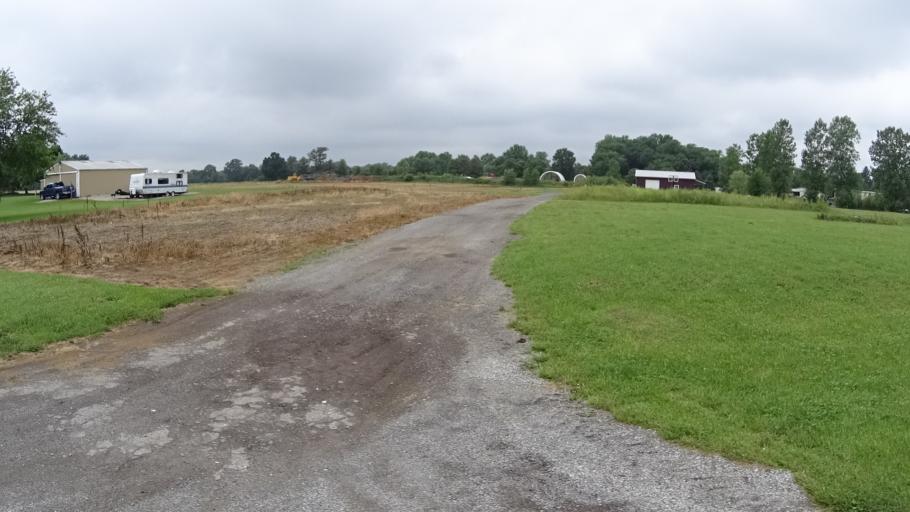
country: US
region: Ohio
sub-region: Erie County
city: Milan
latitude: 41.2980
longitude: -82.5560
